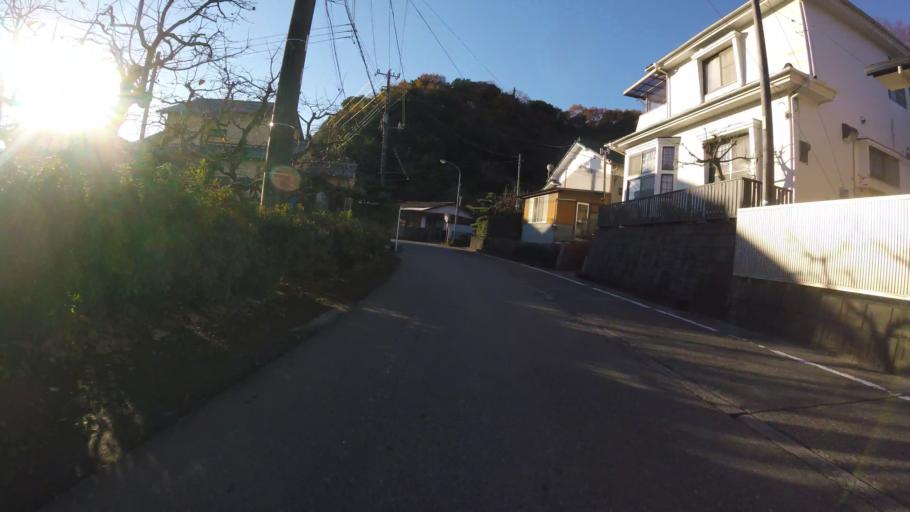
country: JP
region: Shizuoka
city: Mishima
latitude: 35.0261
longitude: 138.9376
